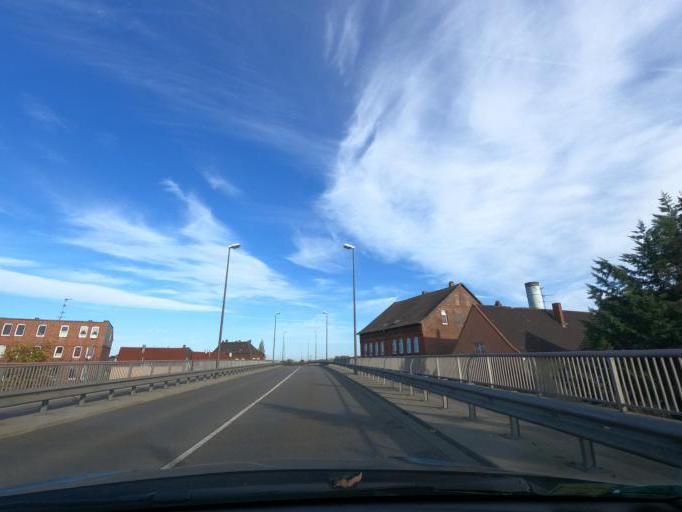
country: DE
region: Lower Saxony
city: Peine
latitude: 52.3172
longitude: 10.2339
